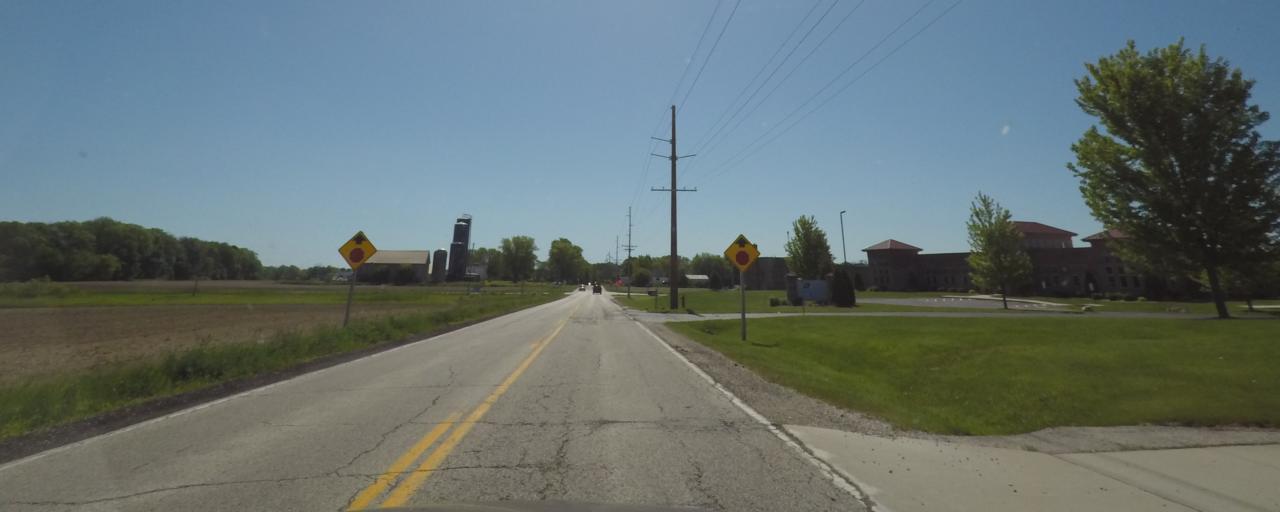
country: US
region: Wisconsin
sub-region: Sheboygan County
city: Sheboygan Falls
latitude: 43.7401
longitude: -87.8524
